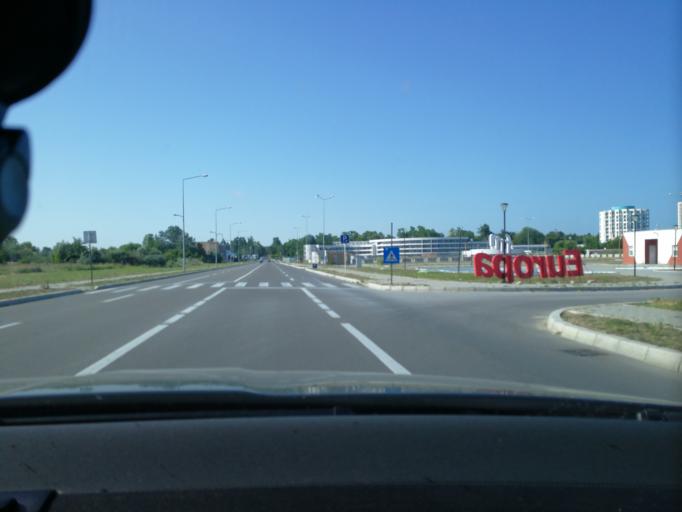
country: RO
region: Constanta
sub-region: Municipiul Mangalia
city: Mangalia
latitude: 43.8411
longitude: 28.5899
